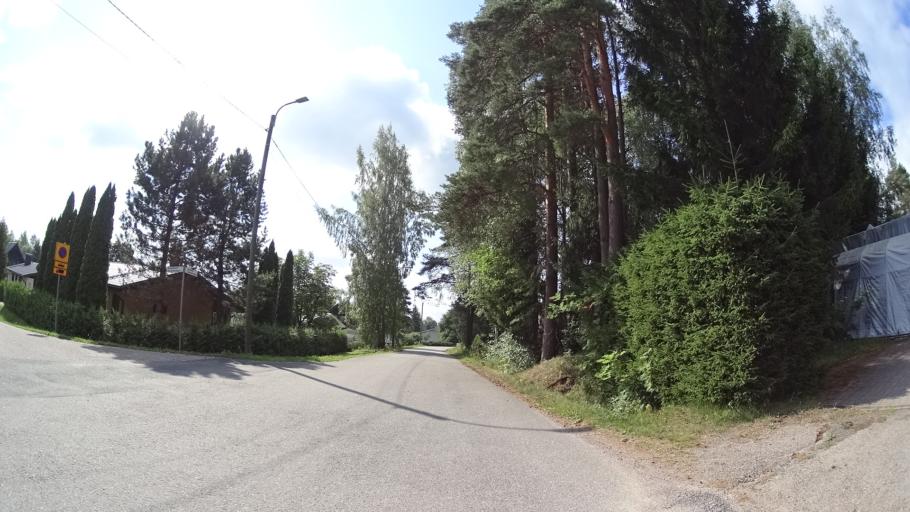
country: FI
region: Uusimaa
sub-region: Helsinki
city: Helsinki
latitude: 60.2834
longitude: 24.9145
